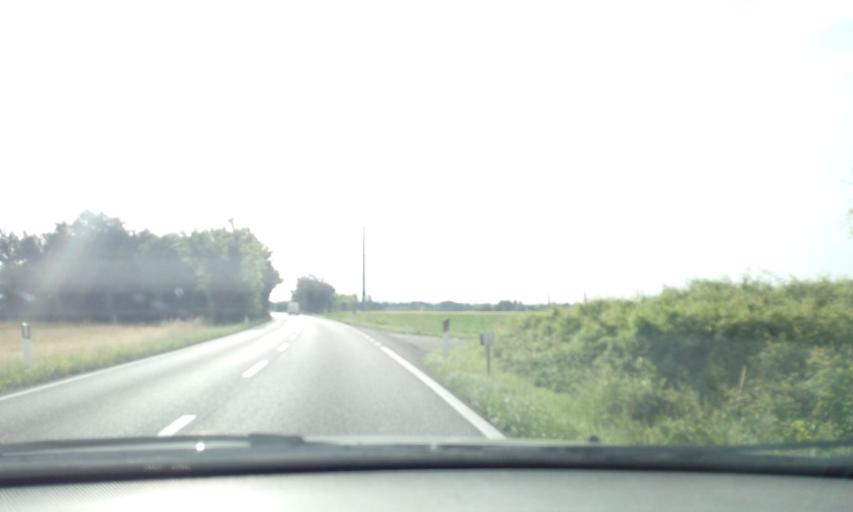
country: IT
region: Friuli Venezia Giulia
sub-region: Provincia di Udine
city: San Vito al Torre
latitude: 45.8919
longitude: 13.3892
